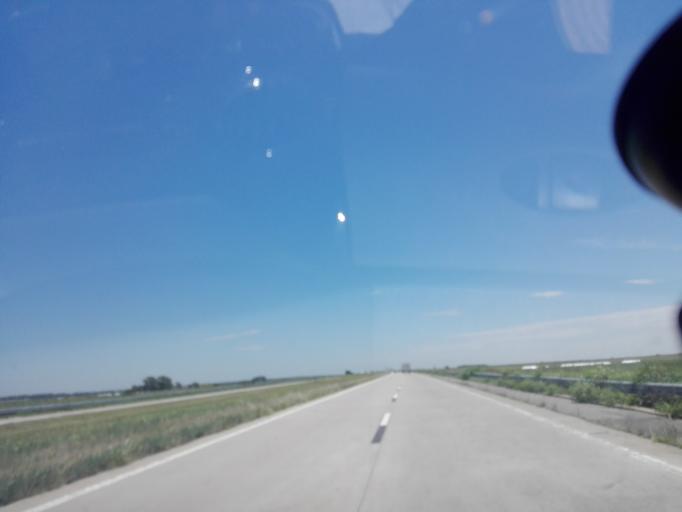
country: AR
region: Cordoba
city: Morrison
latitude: -32.5238
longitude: -62.9470
